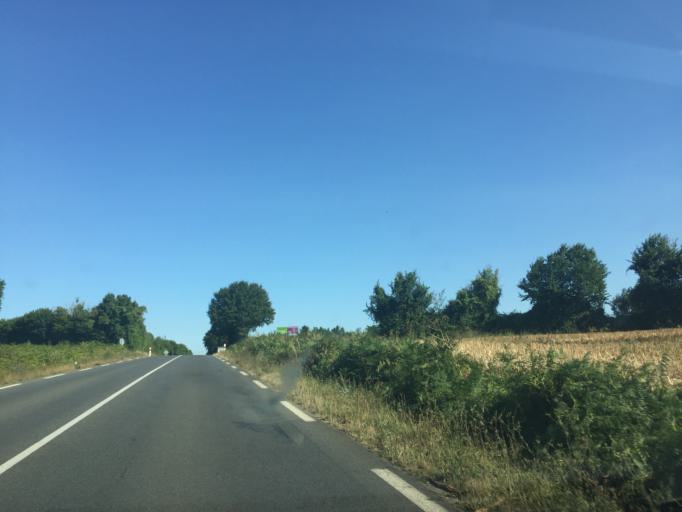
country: FR
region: Poitou-Charentes
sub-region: Departement des Deux-Sevres
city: Chef-Boutonne
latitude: 46.1932
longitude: -0.0620
